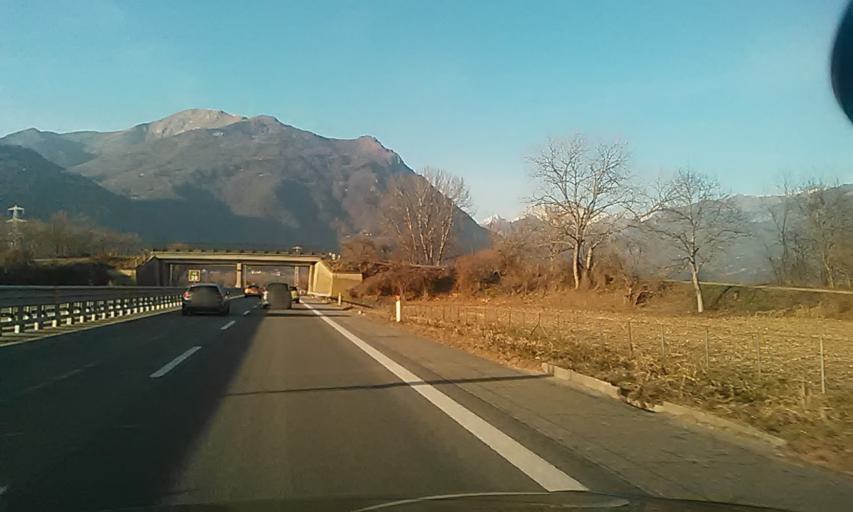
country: IT
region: Piedmont
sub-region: Provincia di Torino
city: Fiorano Canavese
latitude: 45.4747
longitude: 7.8408
